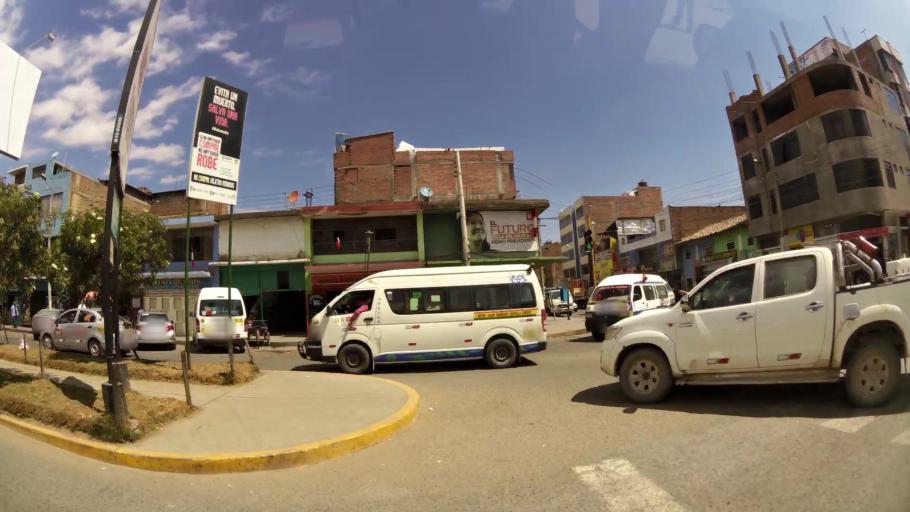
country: PE
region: Junin
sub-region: Provincia de Huancayo
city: Huancayo
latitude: -12.0725
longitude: -75.2034
